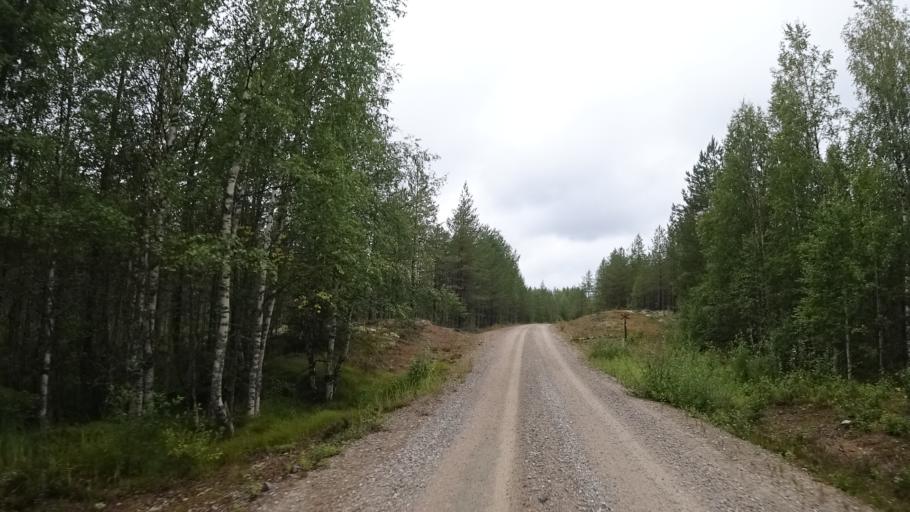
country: FI
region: North Karelia
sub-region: Pielisen Karjala
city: Lieksa
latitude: 63.5144
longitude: 30.1238
